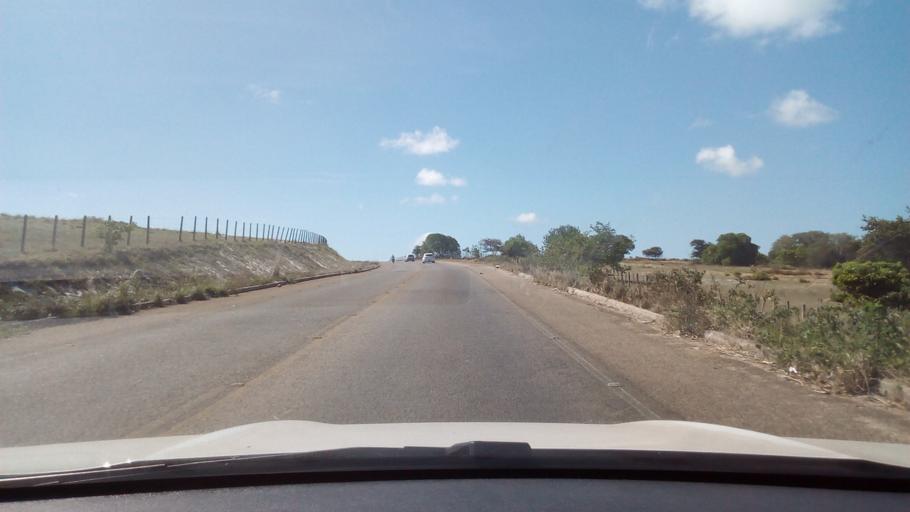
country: BR
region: Rio Grande do Norte
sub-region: Ares
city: Ares
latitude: -6.2280
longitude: -35.0832
